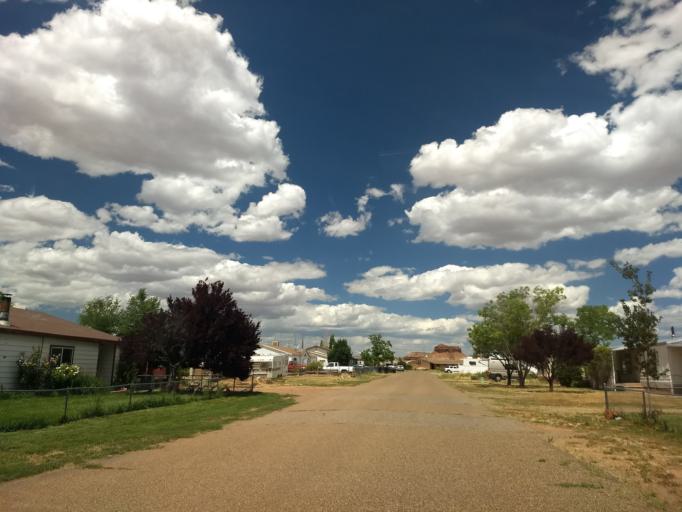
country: US
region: Arizona
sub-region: Coconino County
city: Fredonia
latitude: 36.9596
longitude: -112.5256
